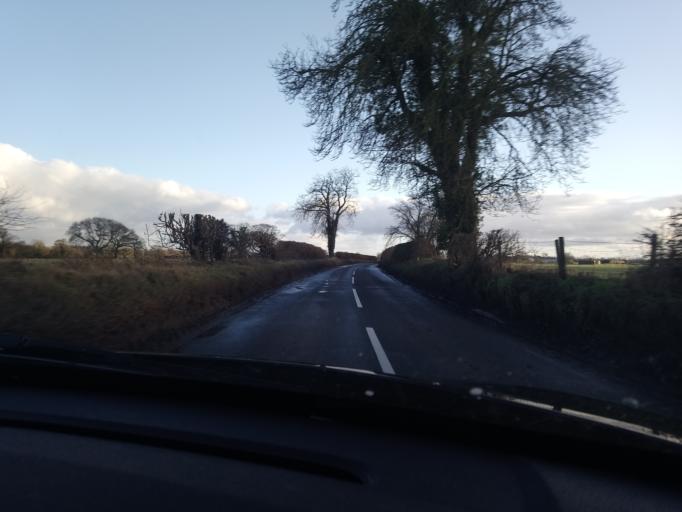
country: GB
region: England
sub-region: Shropshire
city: Petton
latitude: 52.8817
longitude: -2.7858
